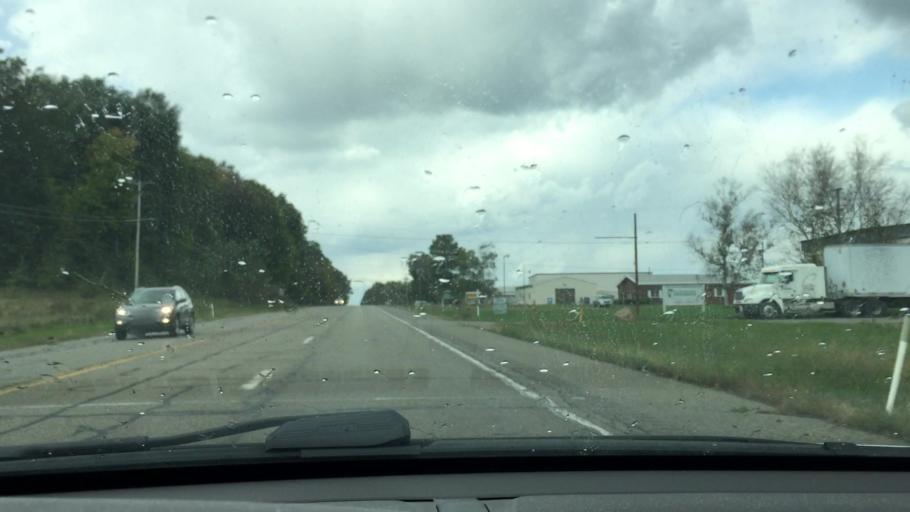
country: US
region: Pennsylvania
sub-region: Lawrence County
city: Oakwood
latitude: 41.0589
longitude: -80.4501
